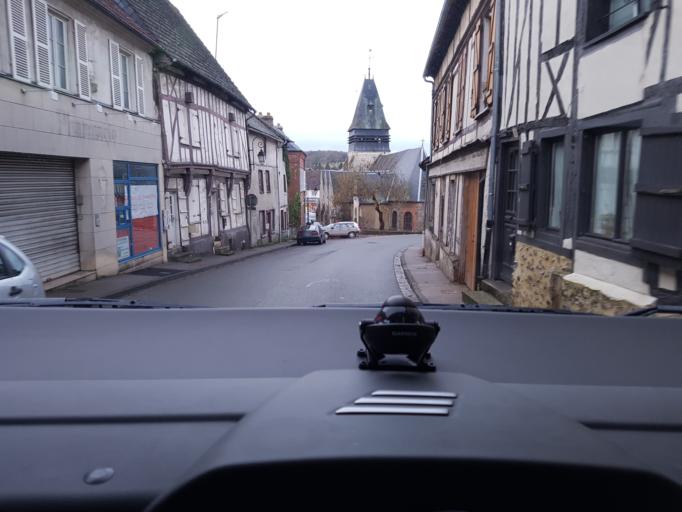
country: FR
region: Picardie
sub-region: Departement de l'Oise
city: Songeons
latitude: 49.5477
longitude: 1.8549
